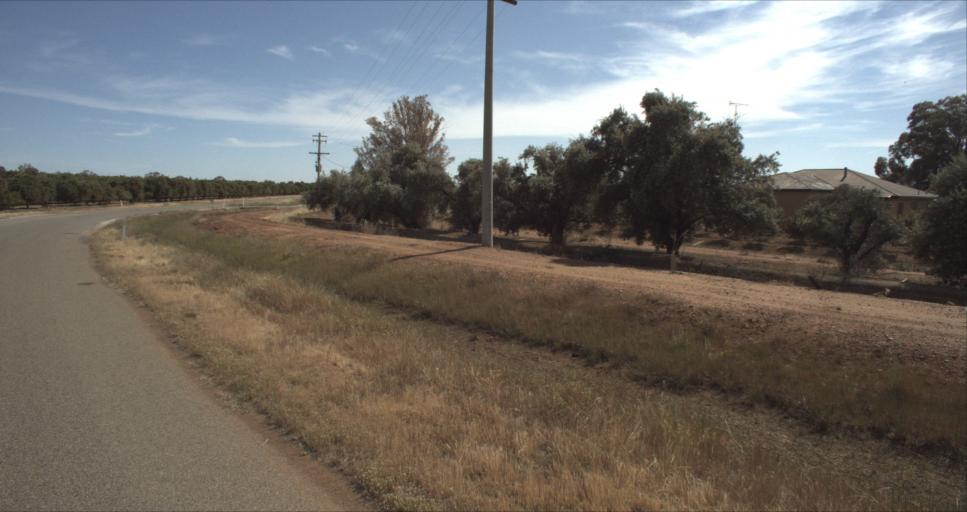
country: AU
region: New South Wales
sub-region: Leeton
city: Leeton
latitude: -34.5879
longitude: 146.4614
